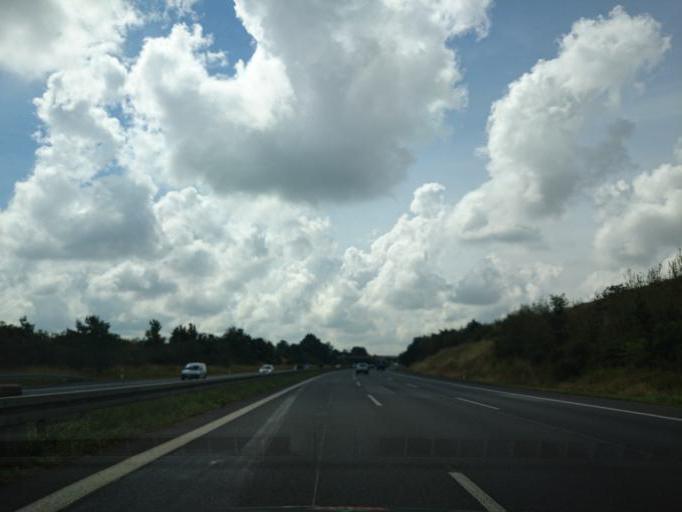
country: DE
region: Brandenburg
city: Schulzendorf
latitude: 52.3473
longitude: 13.5547
